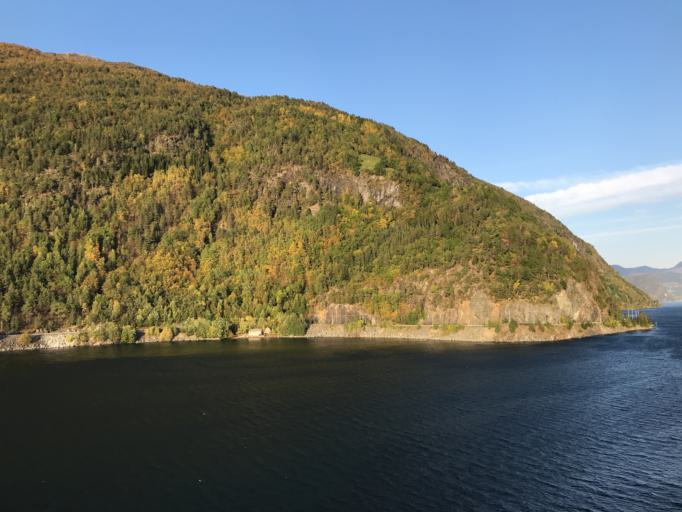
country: NO
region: Sogn og Fjordane
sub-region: Gloppen
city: Sandane
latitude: 61.8451
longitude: 6.1280
